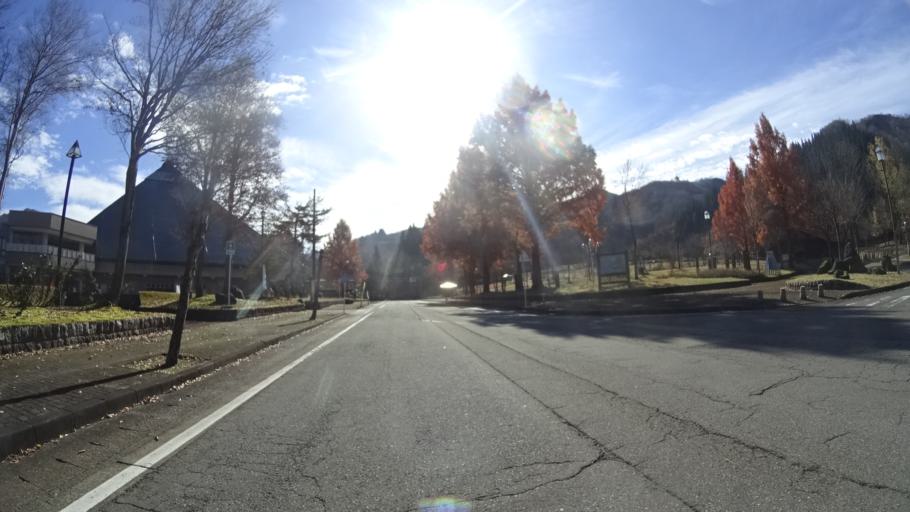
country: JP
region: Niigata
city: Muikamachi
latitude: 37.1981
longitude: 139.0770
